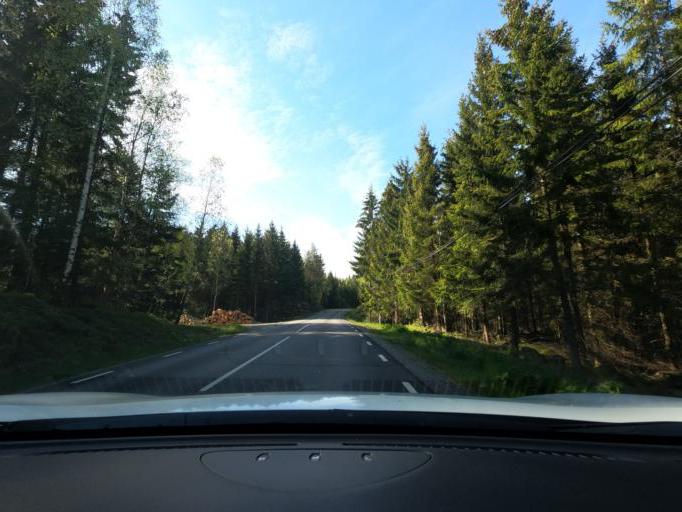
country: SE
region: Vaestra Goetaland
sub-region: Harryda Kommun
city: Landvetter
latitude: 57.6186
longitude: 12.2799
